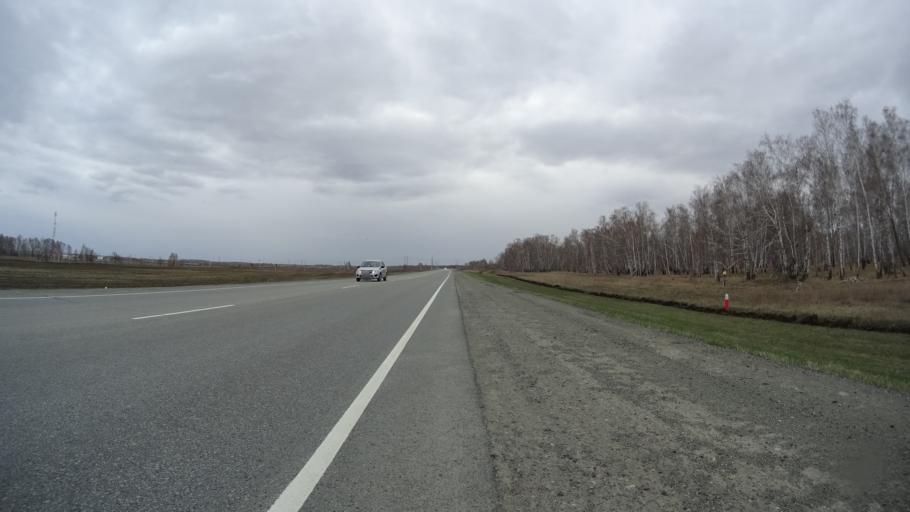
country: RU
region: Chelyabinsk
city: Krasnogorskiy
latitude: 54.6883
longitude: 61.2482
